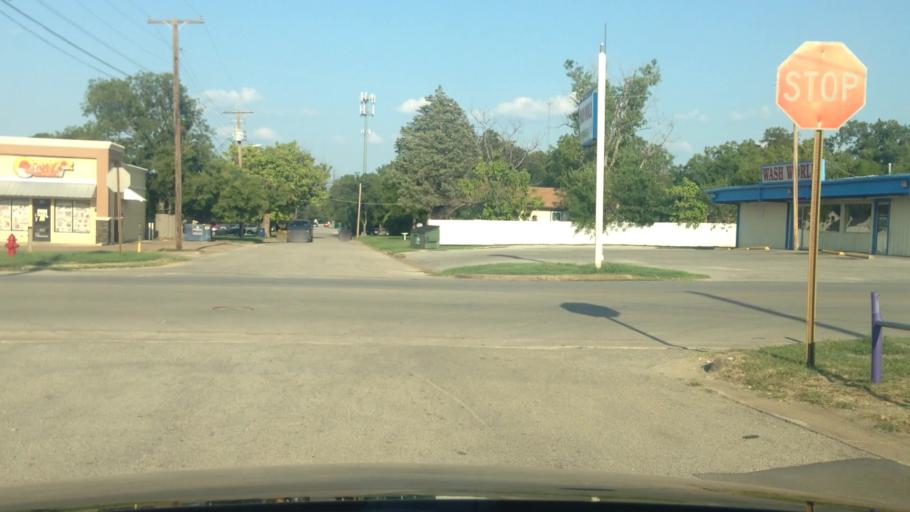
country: US
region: Texas
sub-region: Tarrant County
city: Everman
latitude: 32.6320
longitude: -97.2894
